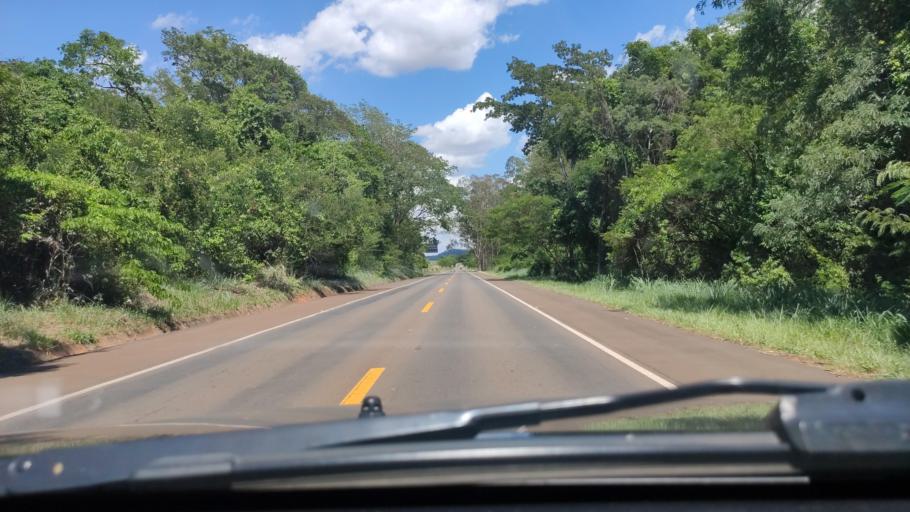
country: BR
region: Sao Paulo
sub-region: Boa Esperanca Do Sul
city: Boa Esperanca do Sul
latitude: -22.0698
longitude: -48.4204
